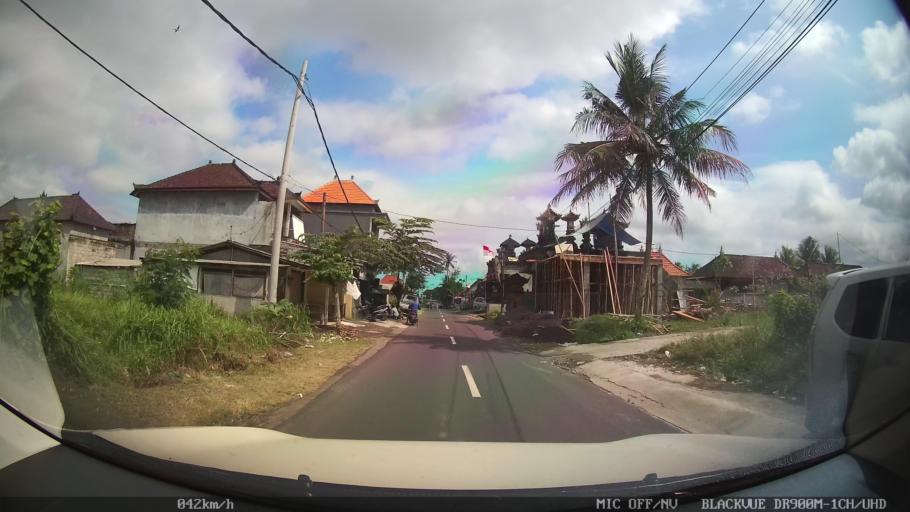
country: ID
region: Bali
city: Banjar Pesalakan
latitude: -8.5202
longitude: 115.3116
